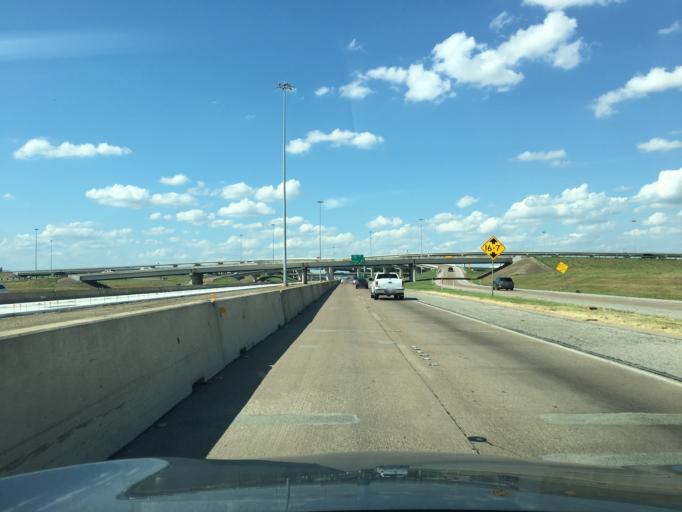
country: US
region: Texas
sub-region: Tarrant County
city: Arlington
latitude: 32.6719
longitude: -97.0625
